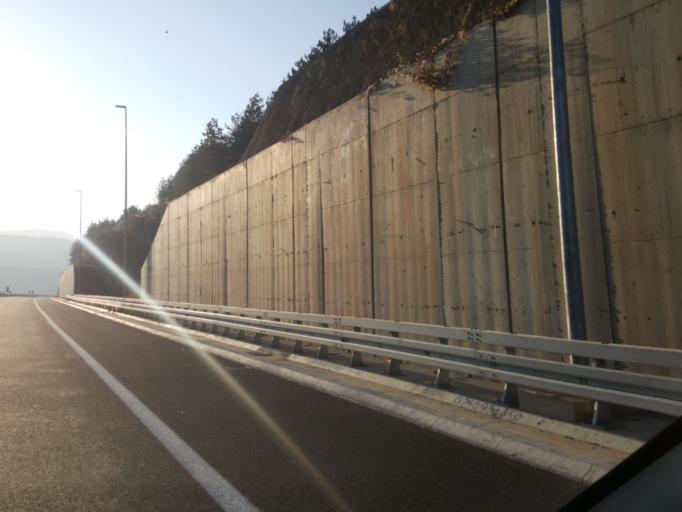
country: RS
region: Central Serbia
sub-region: Pirotski Okrug
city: Dimitrovgrad
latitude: 43.0189
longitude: 22.7676
